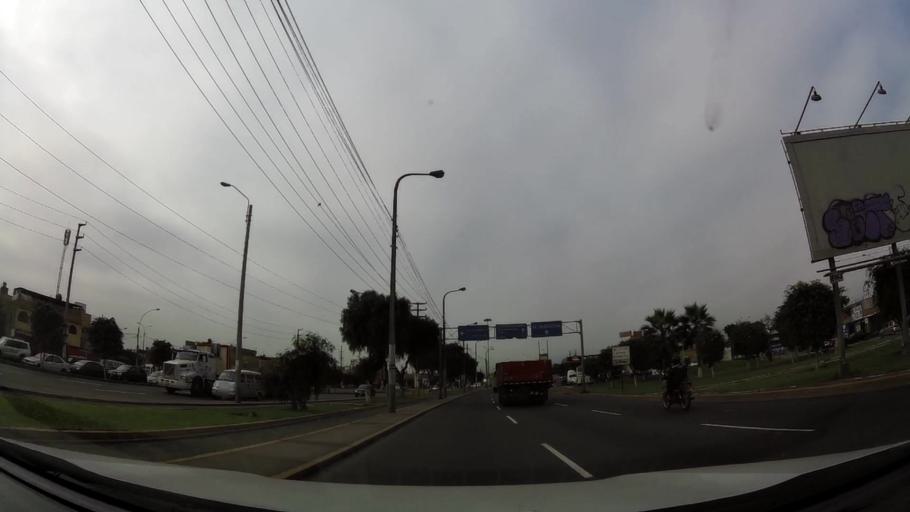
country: PE
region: Callao
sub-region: Callao
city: Callao
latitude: -12.0145
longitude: -77.0960
